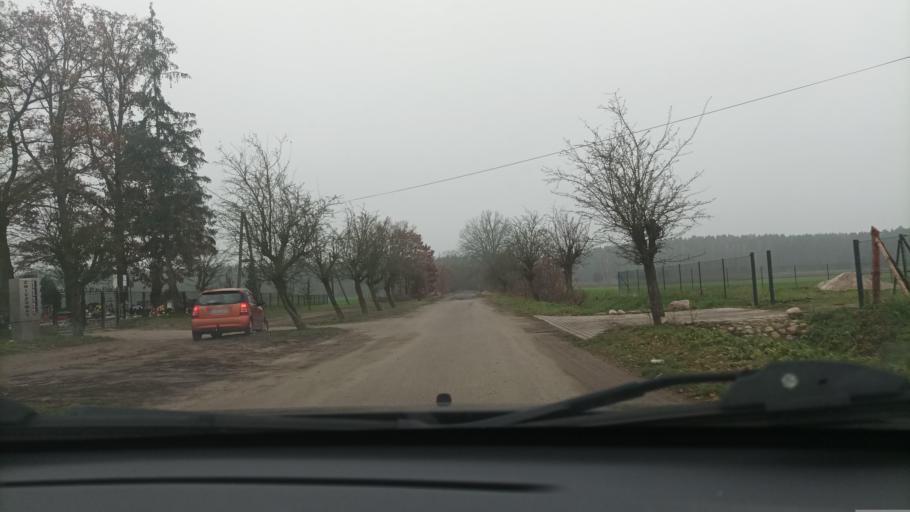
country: PL
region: Greater Poland Voivodeship
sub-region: Powiat obornicki
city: Ryczywol
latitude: 52.7555
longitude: 16.8153
